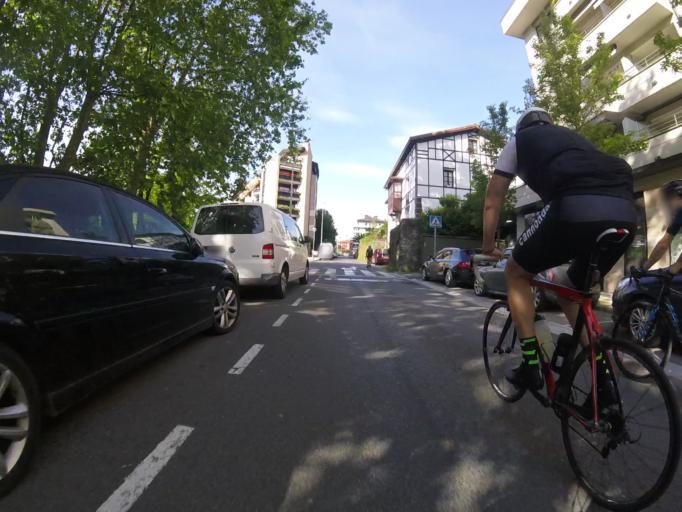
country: ES
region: Basque Country
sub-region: Provincia de Guipuzcoa
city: Villafranca de Ordizia
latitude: 43.0560
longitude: -2.1758
